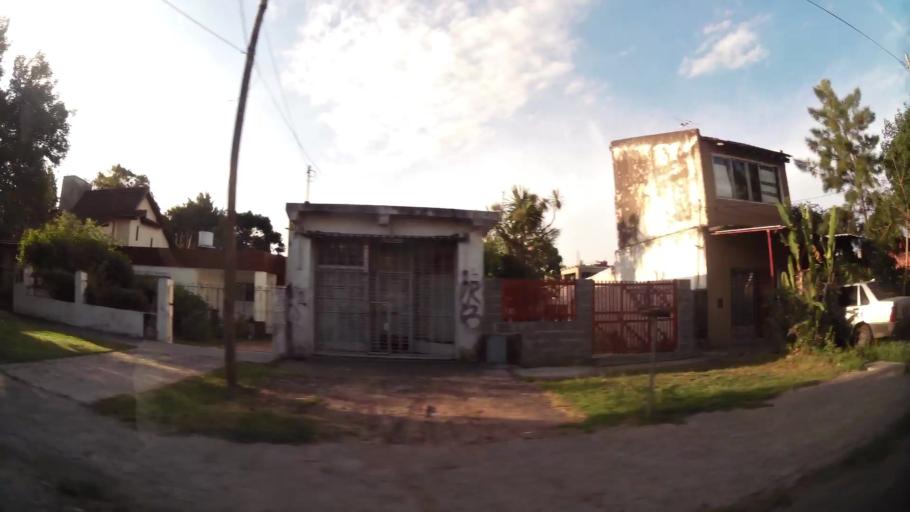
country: AR
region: Buenos Aires
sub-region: Partido de Tigre
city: Tigre
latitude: -34.4529
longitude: -58.6407
